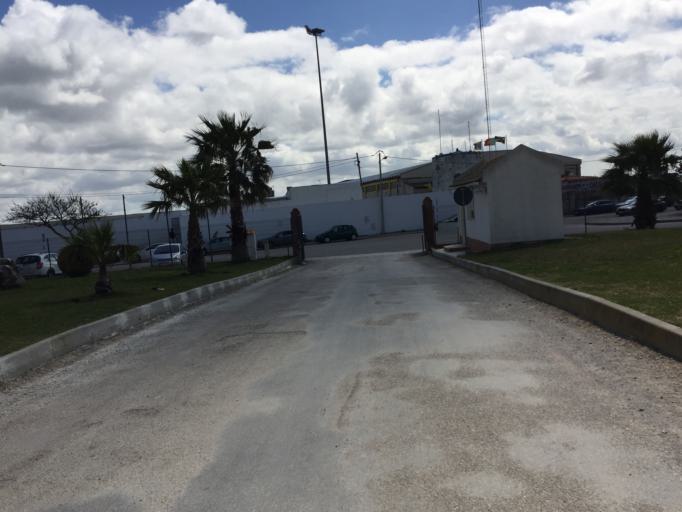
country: PT
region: Setubal
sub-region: Almada
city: Pragal
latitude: 38.6772
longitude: -9.1707
